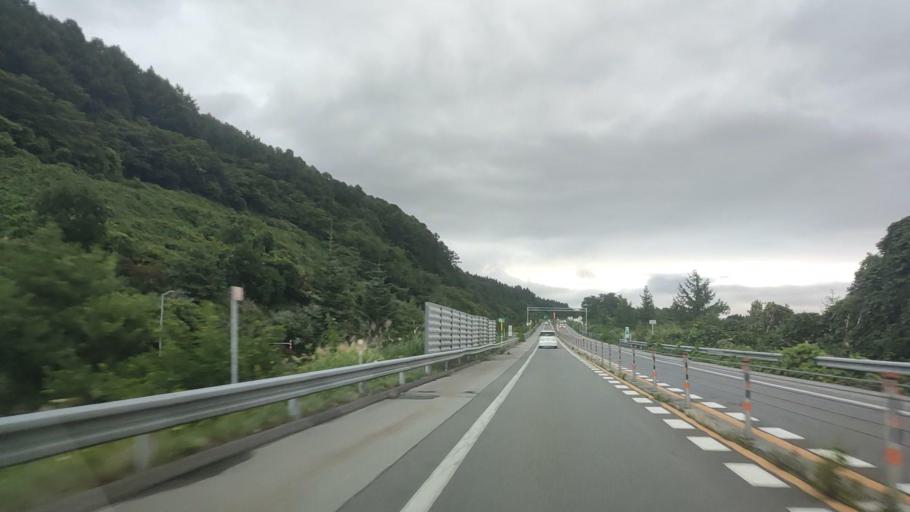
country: JP
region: Hokkaido
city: Nanae
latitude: 41.9124
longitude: 140.6920
